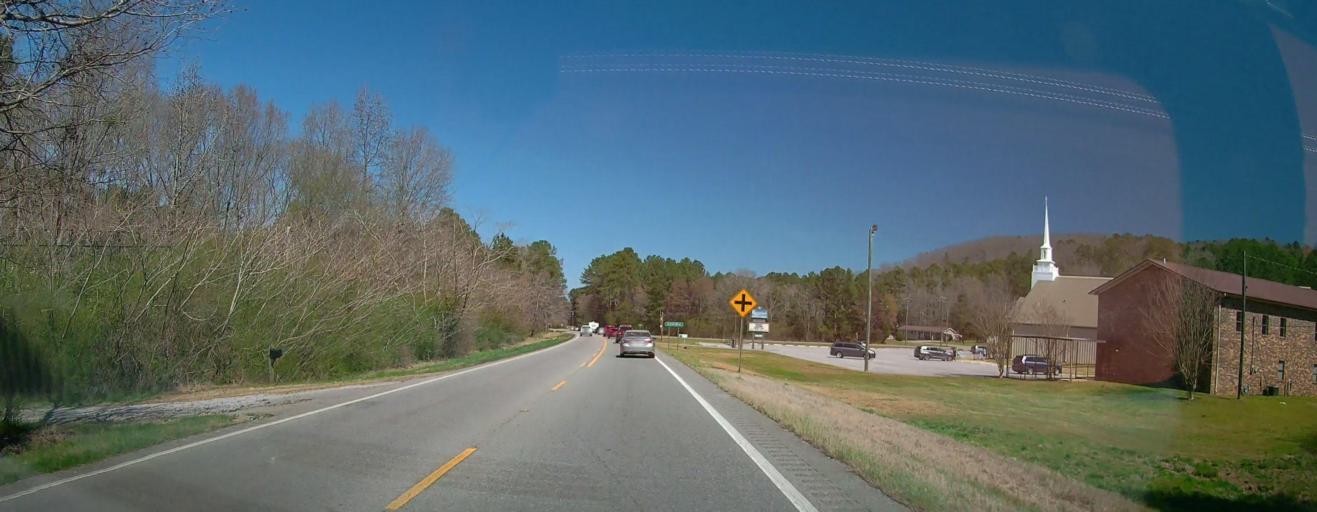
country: US
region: Alabama
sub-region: Etowah County
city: Southside
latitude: 33.8809
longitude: -86.0321
